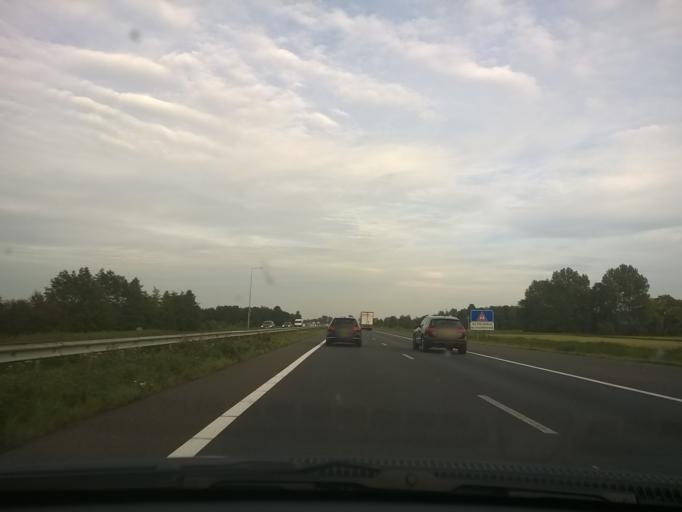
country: NL
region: Groningen
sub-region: Gemeente Zuidhorn
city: Zuidhorn
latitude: 53.1948
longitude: 6.4262
